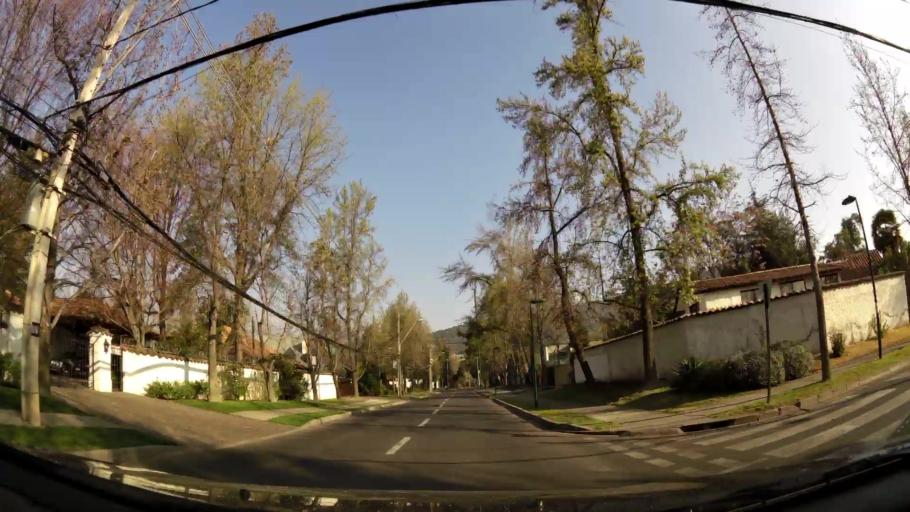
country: CL
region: Santiago Metropolitan
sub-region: Provincia de Santiago
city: Villa Presidente Frei, Nunoa, Santiago, Chile
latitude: -33.3603
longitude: -70.5302
